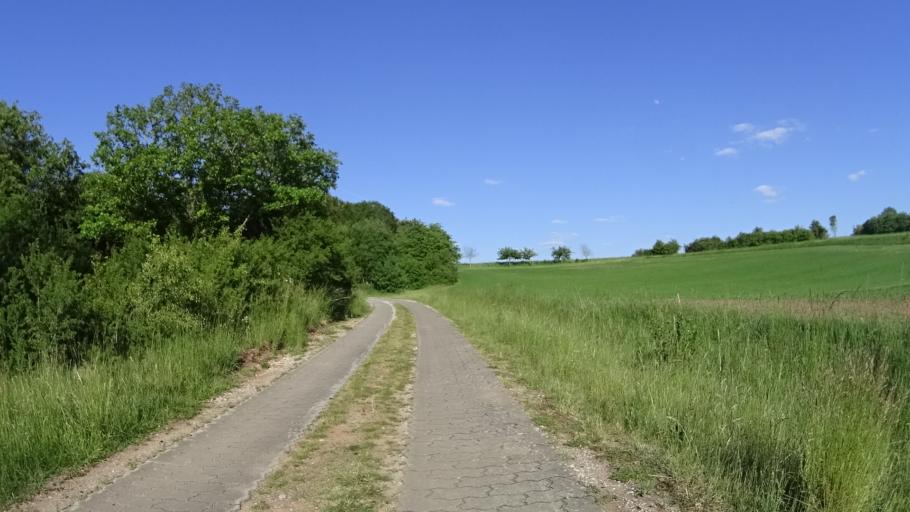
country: DE
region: Bavaria
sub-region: Regierungsbezirk Mittelfranken
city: Lichtenau
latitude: 49.1622
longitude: 10.3612
